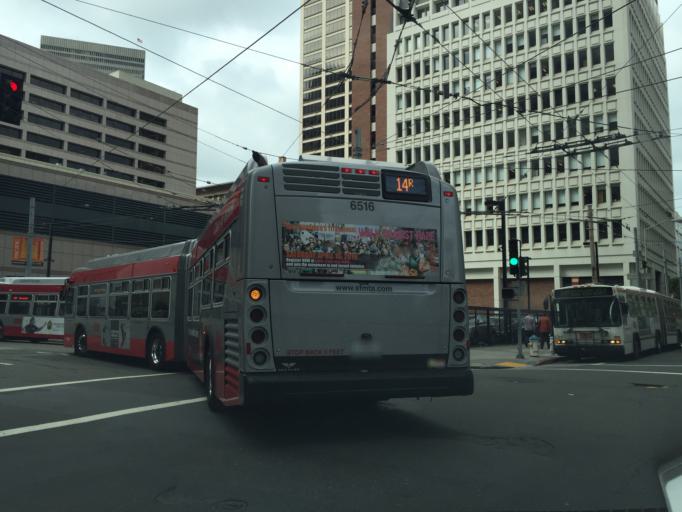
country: US
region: California
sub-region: San Francisco County
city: San Francisco
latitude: 37.7917
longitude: -122.3950
